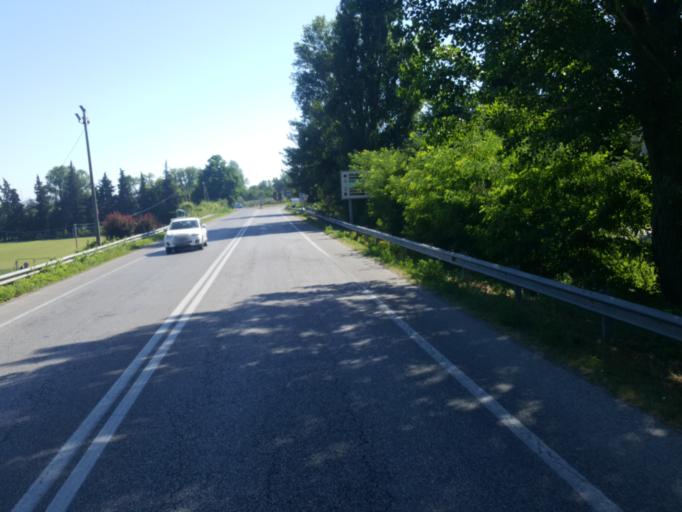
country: IT
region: The Marches
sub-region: Provincia di Pesaro e Urbino
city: Montelabbate
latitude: 43.8499
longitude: 12.7856
